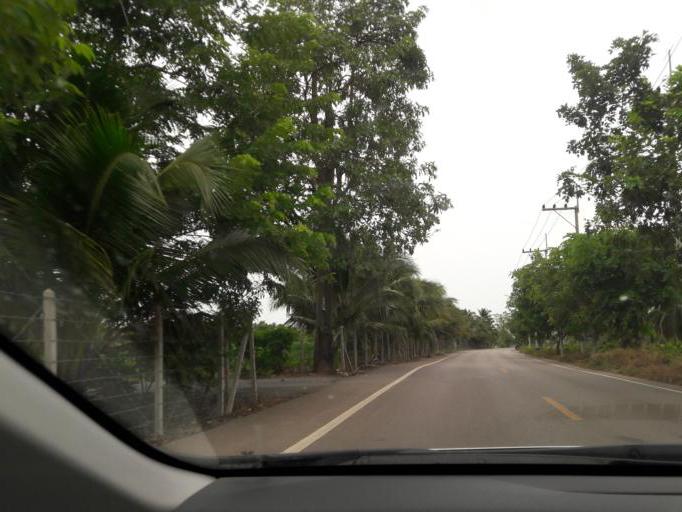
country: TH
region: Samut Sakhon
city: Ban Phaeo
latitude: 13.5680
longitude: 100.0429
